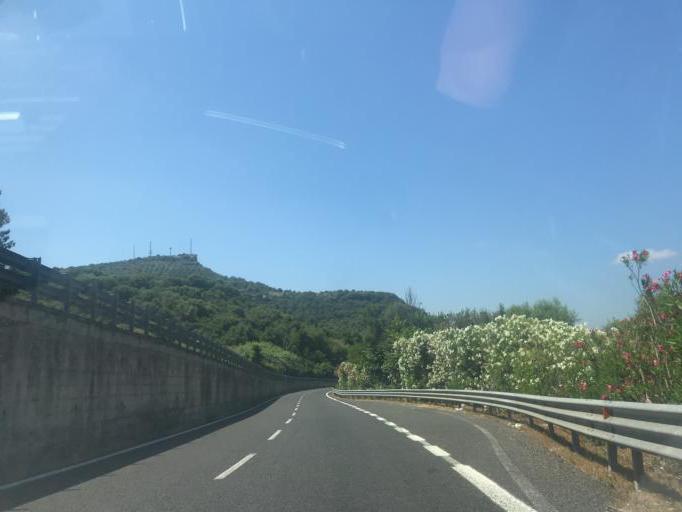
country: IT
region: Sardinia
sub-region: Provincia di Sassari
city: Florinas
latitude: 40.6533
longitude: 8.6731
